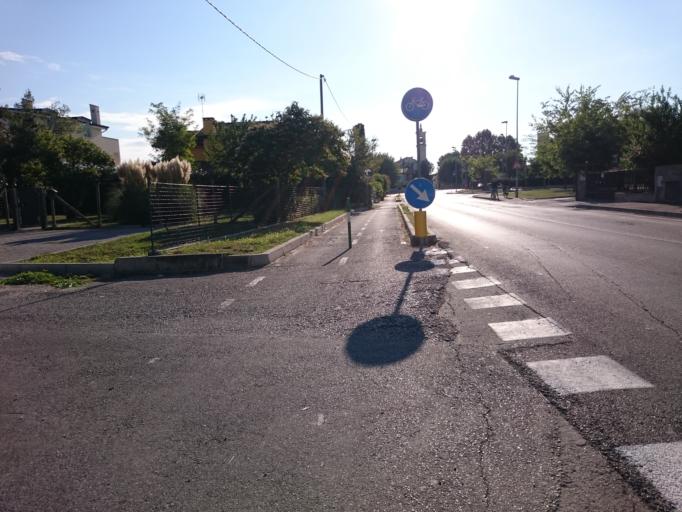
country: IT
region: Veneto
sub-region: Provincia di Padova
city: Albignasego
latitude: 45.3397
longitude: 11.8762
